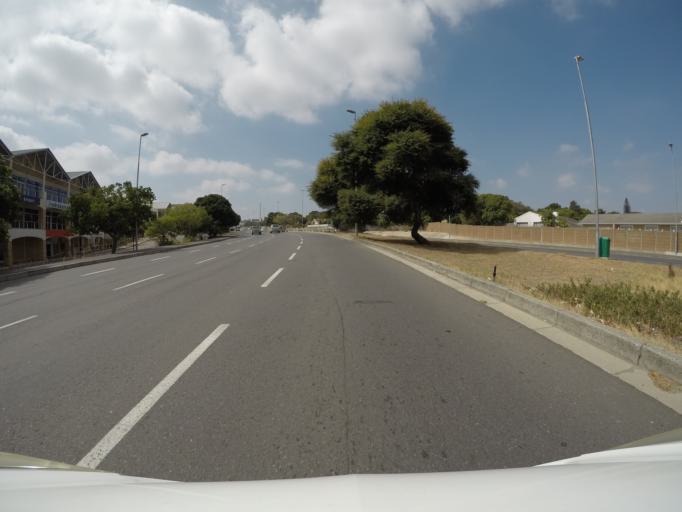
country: ZA
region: Western Cape
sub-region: City of Cape Town
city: Kraaifontein
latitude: -33.8744
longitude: 18.6377
